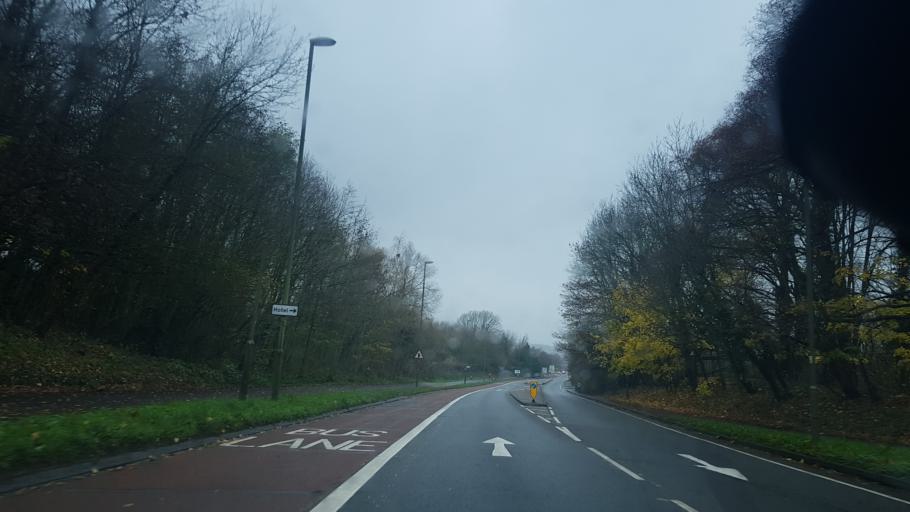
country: GB
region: England
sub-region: Surrey
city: Guildford
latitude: 51.2476
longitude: -0.5638
